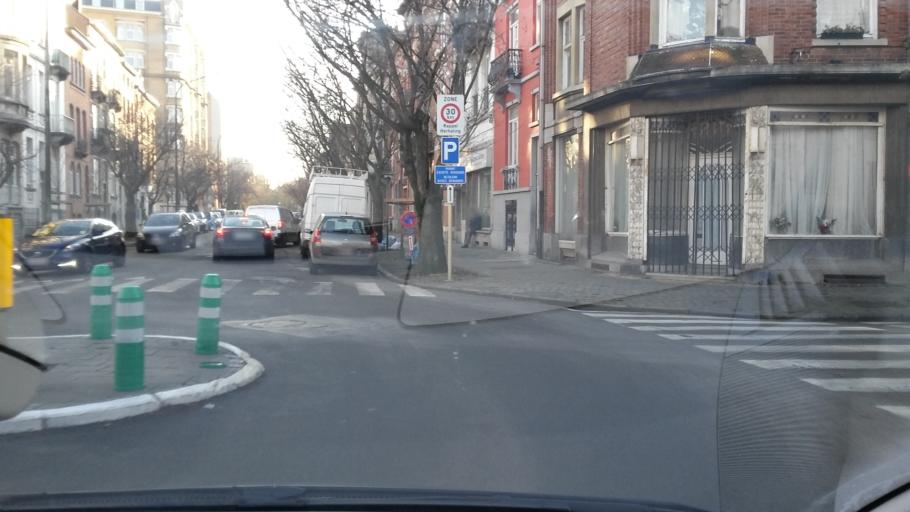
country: BE
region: Brussels Capital
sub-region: Bruxelles-Capitale
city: Brussels
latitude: 50.8519
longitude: 4.3937
